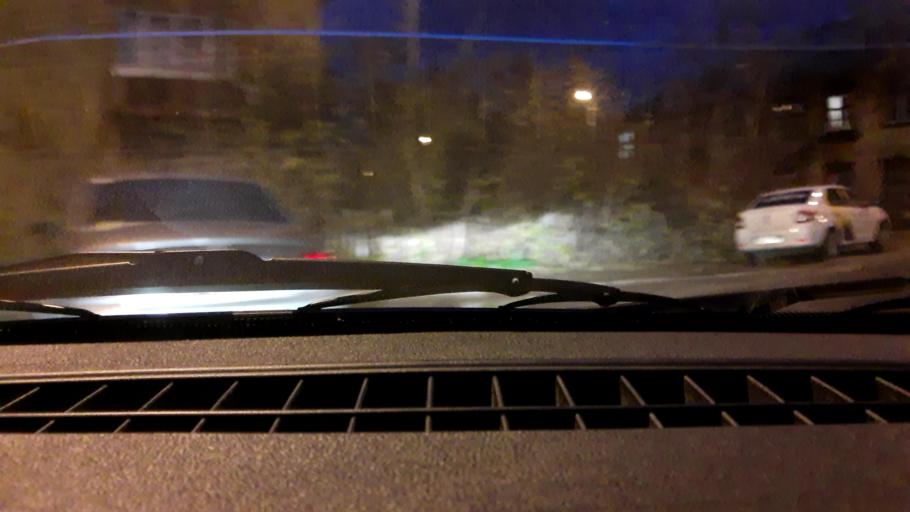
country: RU
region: Bashkortostan
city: Ufa
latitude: 54.7950
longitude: 56.1433
